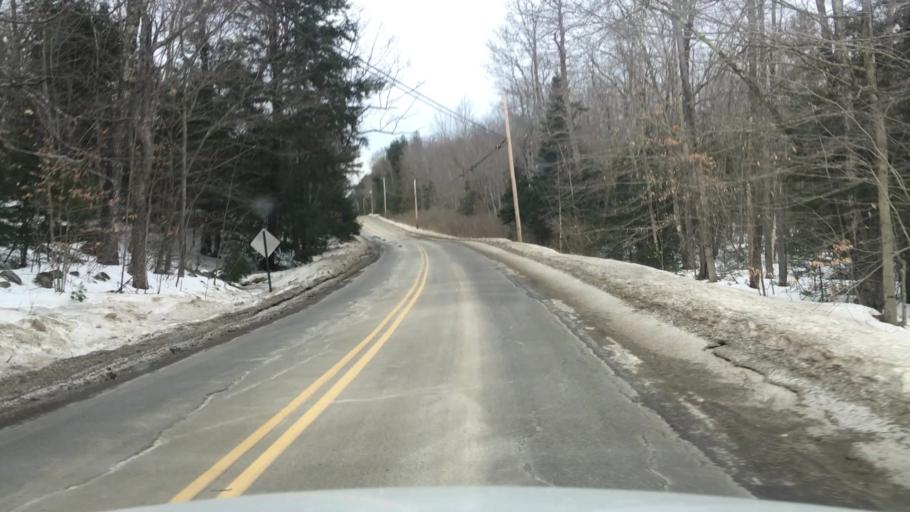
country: US
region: Maine
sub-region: Kennebec County
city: Chelsea
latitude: 44.2594
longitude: -69.6447
